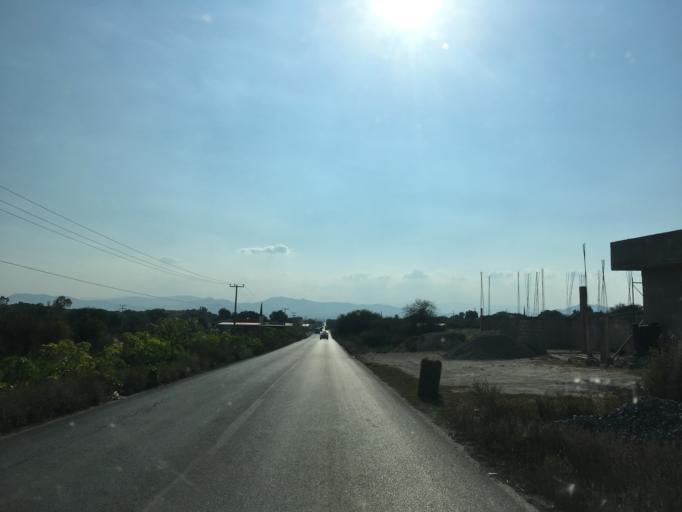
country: MX
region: Hidalgo
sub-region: Ixmiquilpan
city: El Nith
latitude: 20.5564
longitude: -99.1585
